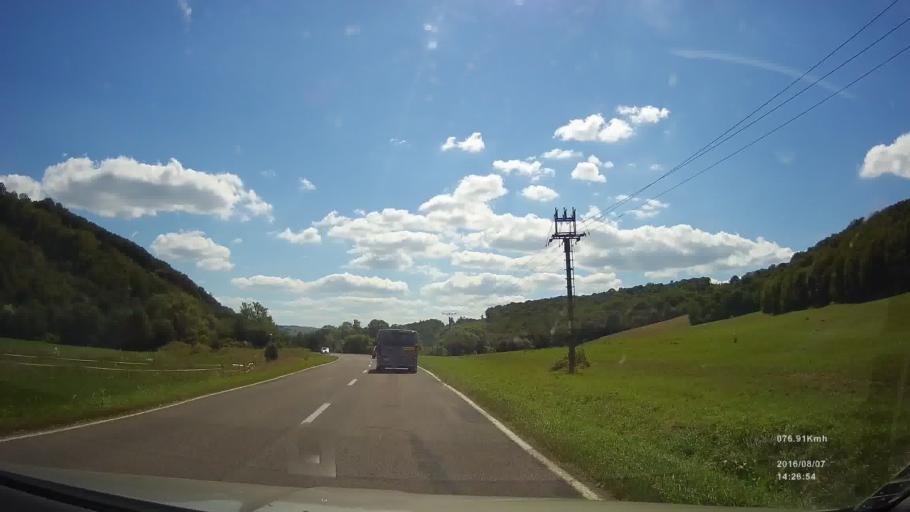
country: SK
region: Presovsky
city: Stropkov
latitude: 49.2646
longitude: 21.6955
